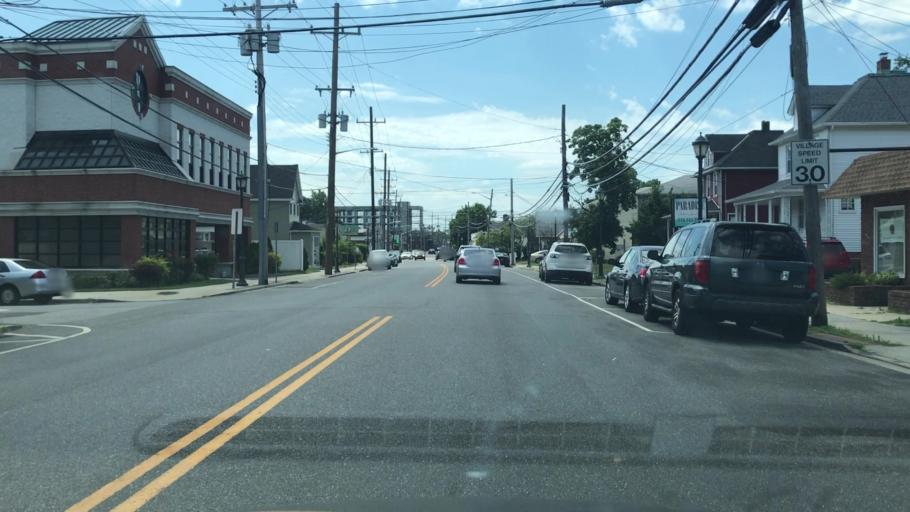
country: US
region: New York
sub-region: Nassau County
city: Valley Stream
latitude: 40.6723
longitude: -73.7091
